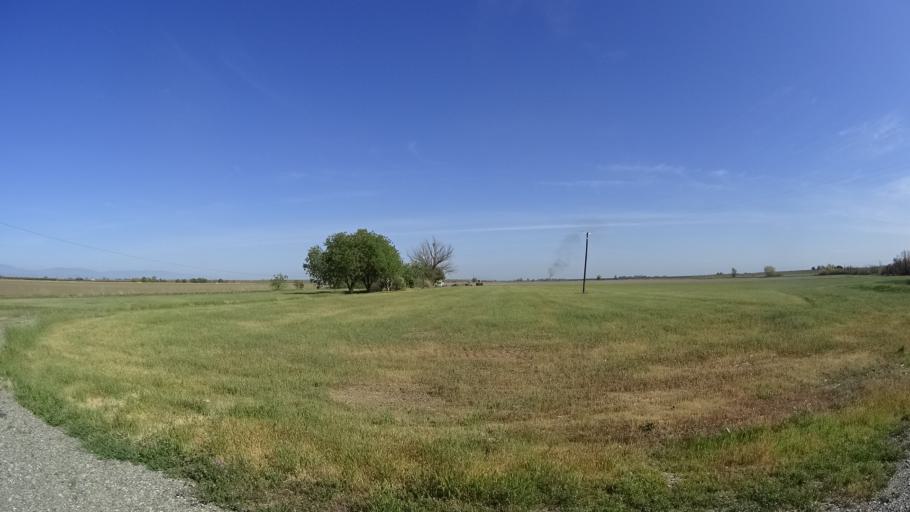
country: US
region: California
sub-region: Glenn County
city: Willows
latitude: 39.5460
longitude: -122.1739
